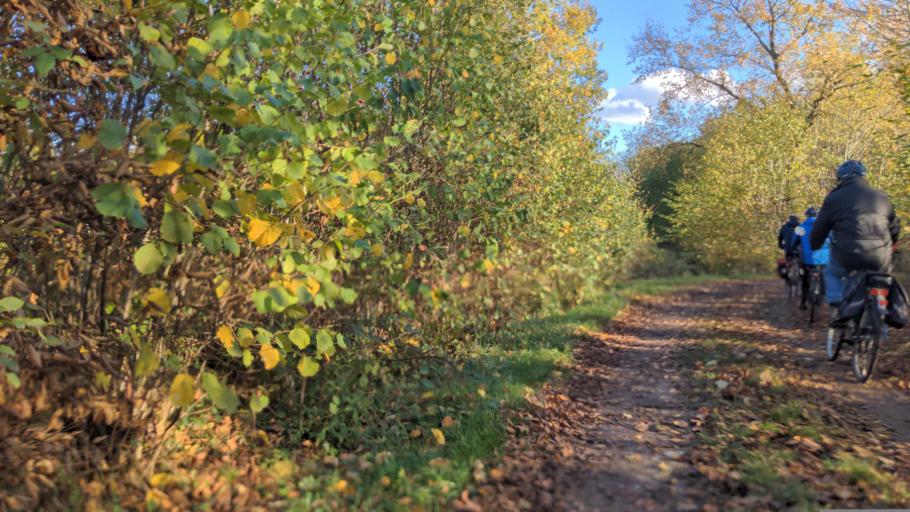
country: DE
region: Schleswig-Holstein
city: Ratekau
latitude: 53.9397
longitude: 10.7705
